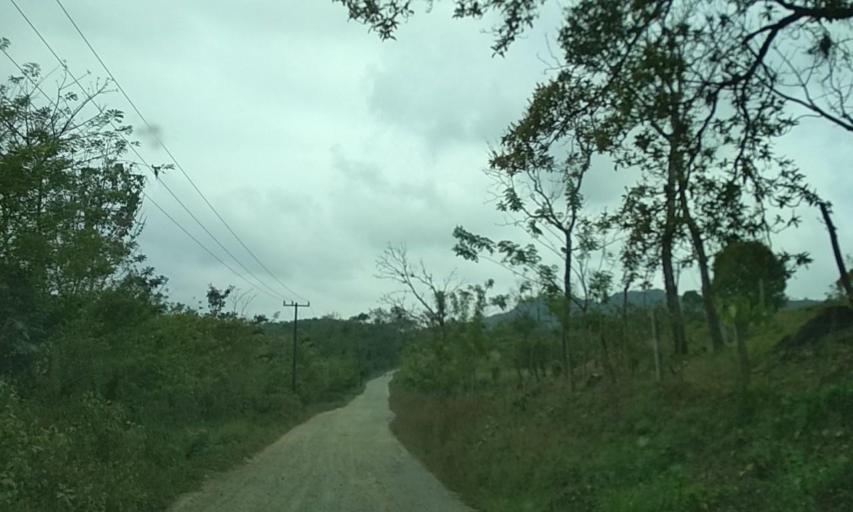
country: MX
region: Veracruz
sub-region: Uxpanapa
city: Poblado 10
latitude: 17.4829
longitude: -94.1269
